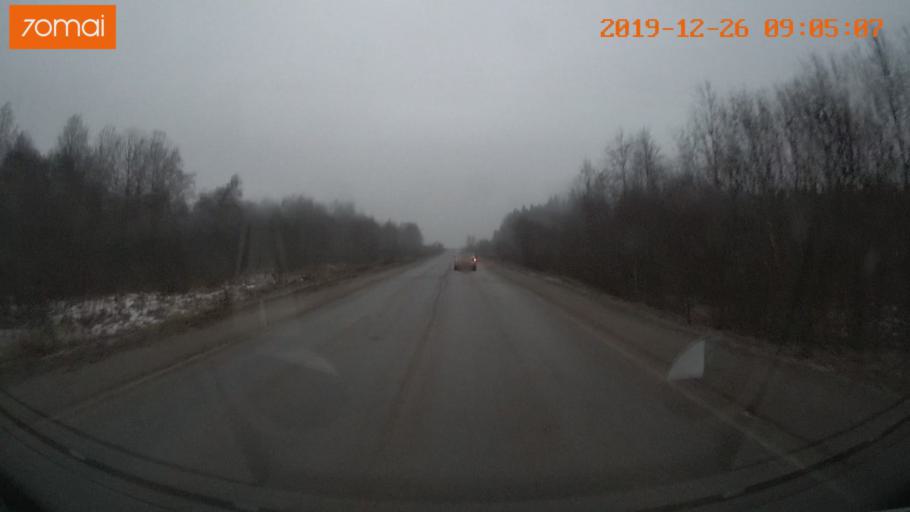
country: RU
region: Vologda
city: Gryazovets
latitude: 58.8222
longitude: 40.2596
